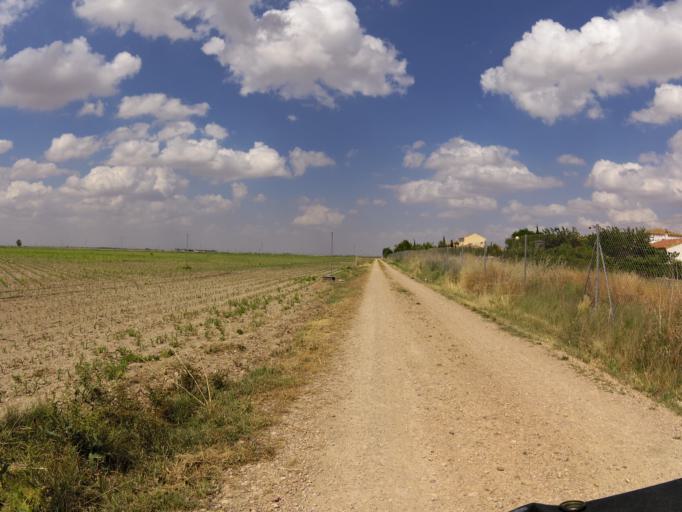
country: ES
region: Castille-La Mancha
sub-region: Provincia de Albacete
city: Pozuelo
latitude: 38.9166
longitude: -2.0111
